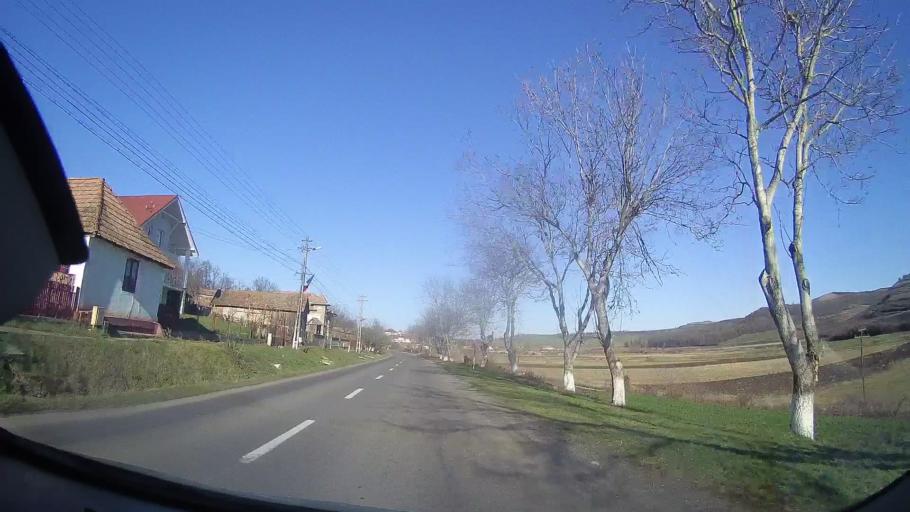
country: RO
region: Mures
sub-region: Comuna Sarmasu
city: Balda
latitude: 46.7260
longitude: 24.1438
